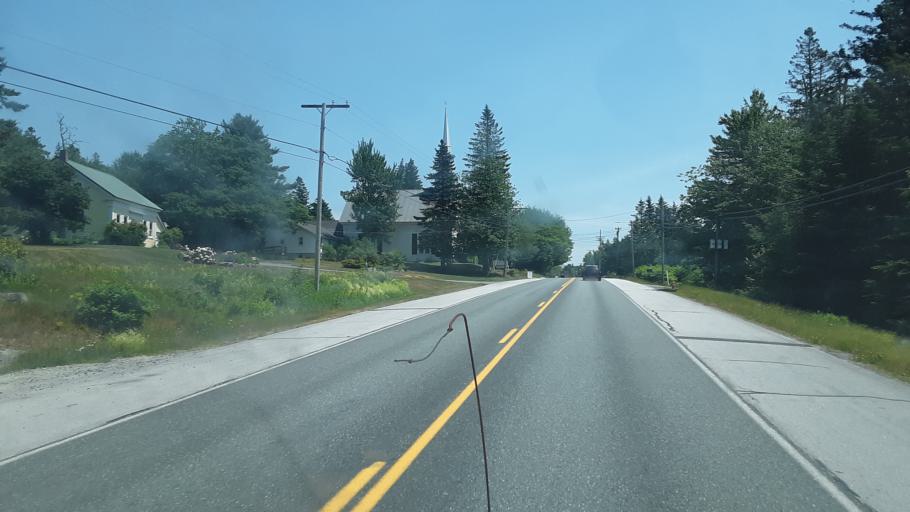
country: US
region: Maine
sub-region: Hancock County
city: Hancock
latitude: 44.5312
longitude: -68.2613
